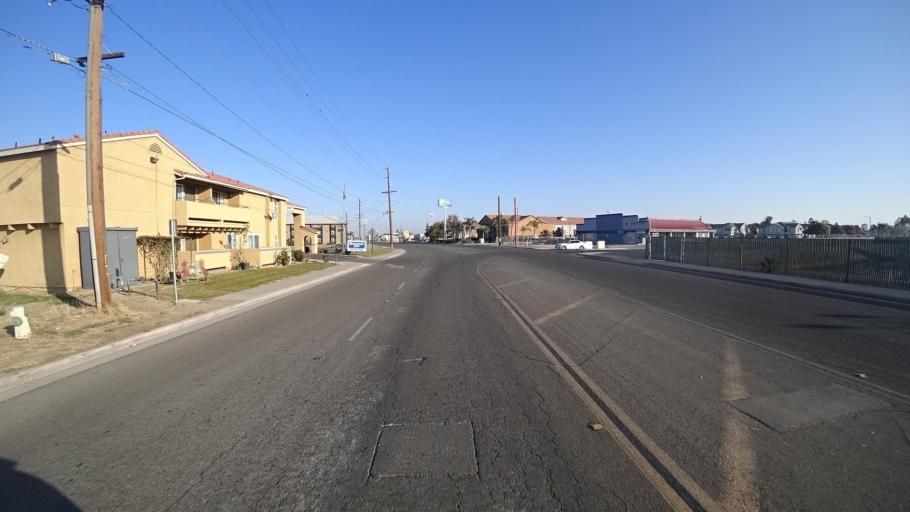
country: US
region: California
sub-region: Kern County
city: Delano
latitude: 35.7868
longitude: -119.2496
